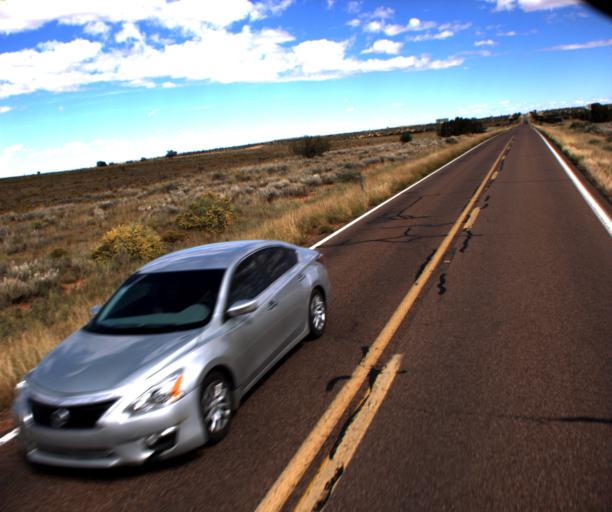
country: US
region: Arizona
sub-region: Navajo County
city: Snowflake
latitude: 34.6500
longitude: -110.3437
